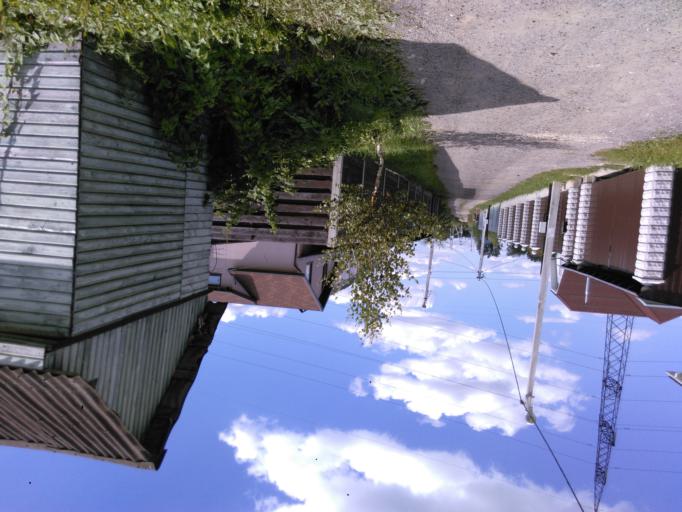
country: RU
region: Moskovskaya
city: Solnechnogorsk
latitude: 56.1340
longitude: 36.9120
